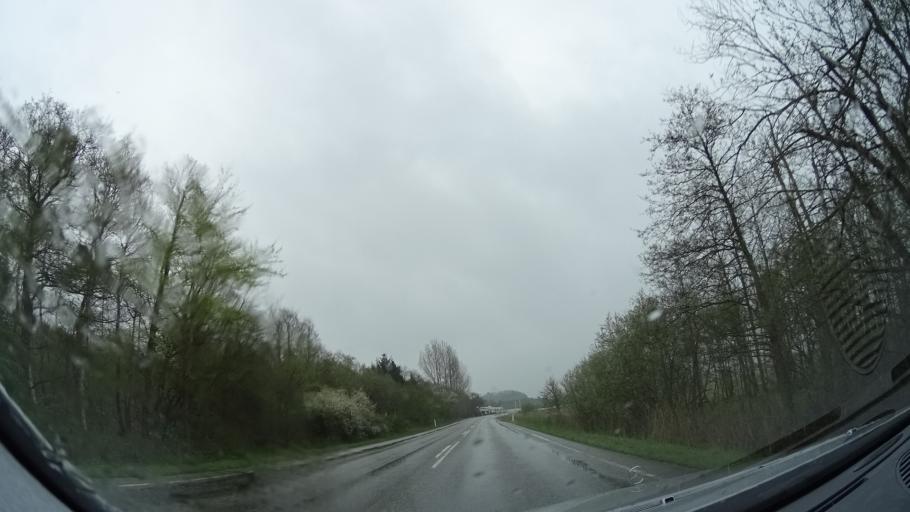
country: DK
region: Zealand
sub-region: Holbaek Kommune
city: Holbaek
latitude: 55.7618
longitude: 11.6297
